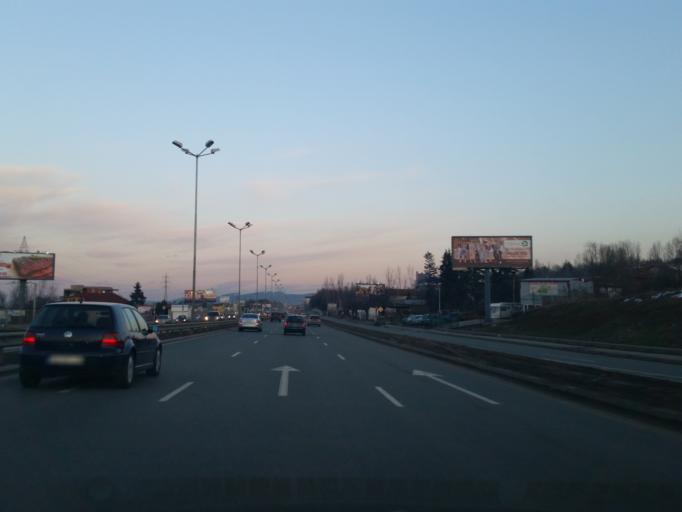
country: BG
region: Sofia-Capital
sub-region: Stolichna Obshtina
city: Sofia
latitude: 42.6497
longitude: 23.2926
